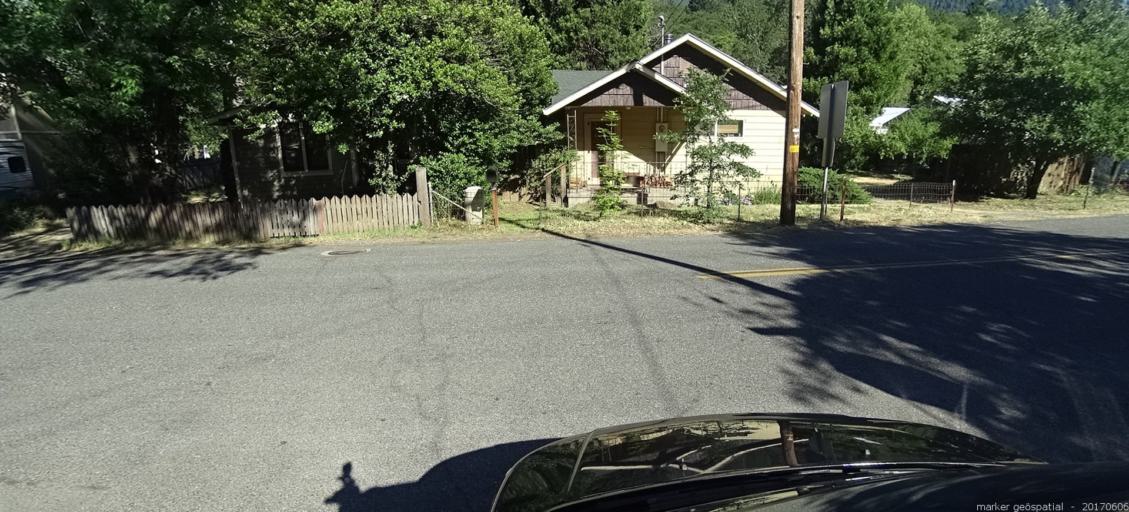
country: US
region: California
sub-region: Siskiyou County
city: Dunsmuir
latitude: 41.2014
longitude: -122.2725
